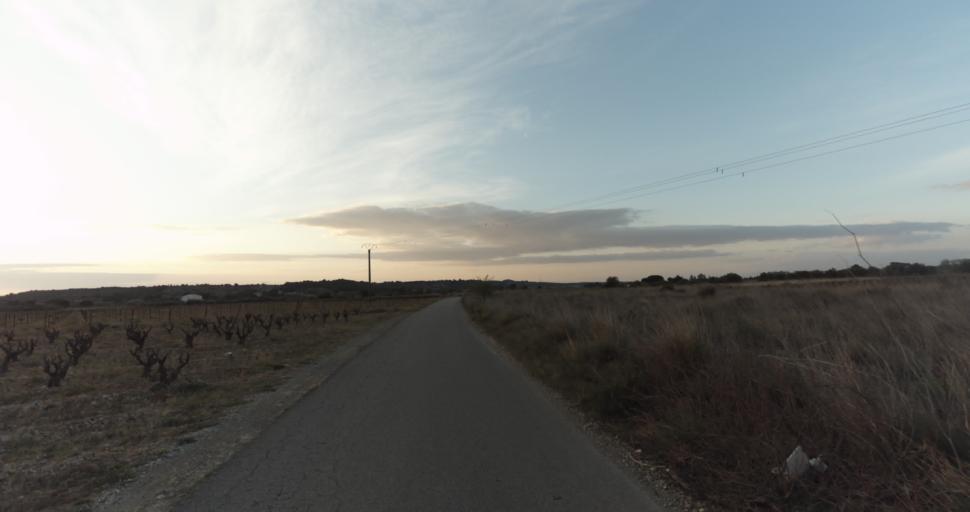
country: FR
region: Languedoc-Roussillon
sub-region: Departement de l'Aude
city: Leucate
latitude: 42.9359
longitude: 3.0017
